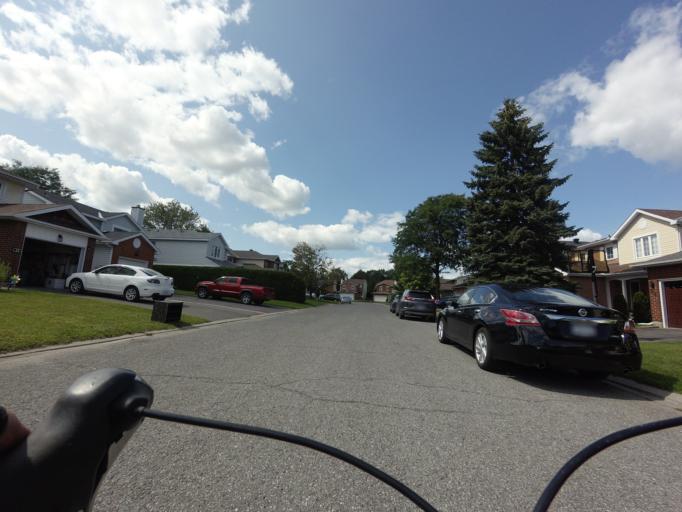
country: CA
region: Ontario
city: Bells Corners
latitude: 45.2950
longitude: -75.8648
